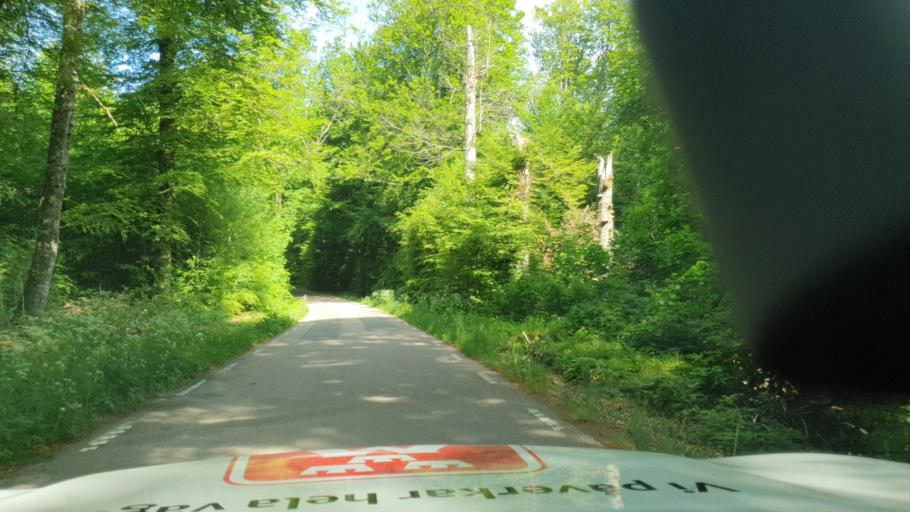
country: SE
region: Vaestra Goetaland
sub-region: Herrljunga Kommun
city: Herrljunga
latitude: 57.9238
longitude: 13.1285
